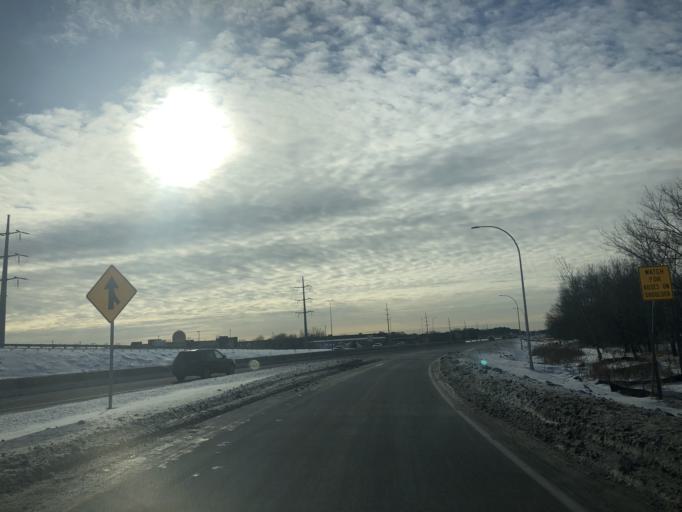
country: US
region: Minnesota
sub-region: Anoka County
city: Lexington
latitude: 45.1588
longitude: -93.1648
